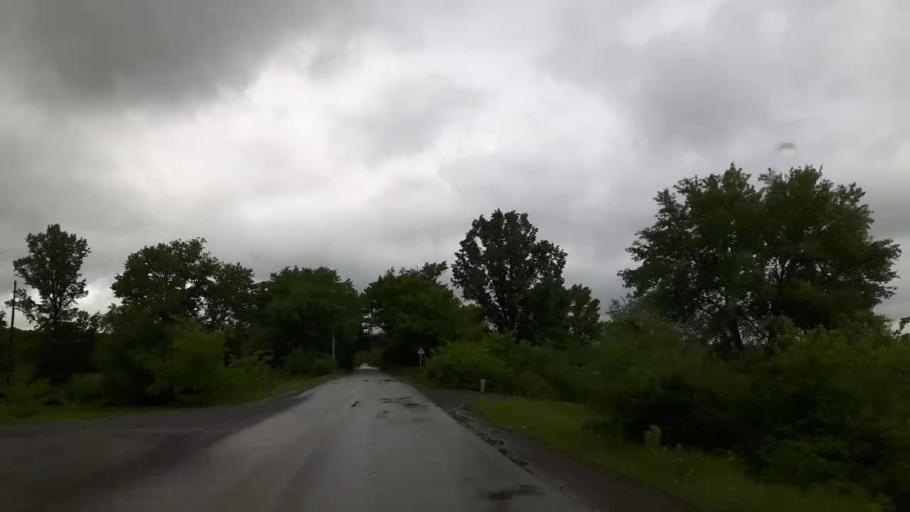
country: GE
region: Shida Kartli
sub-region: Khashuris Raioni
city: Khashuri
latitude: 41.9957
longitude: 43.6561
